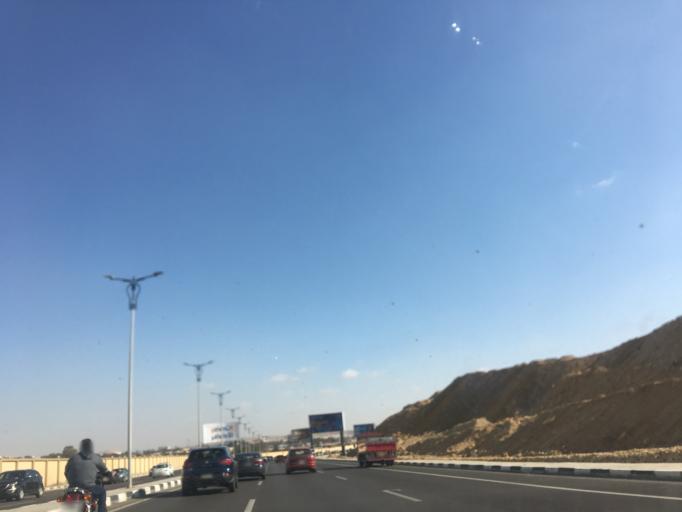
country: EG
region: Muhafazat al Qahirah
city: Cairo
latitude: 30.0266
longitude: 31.3187
